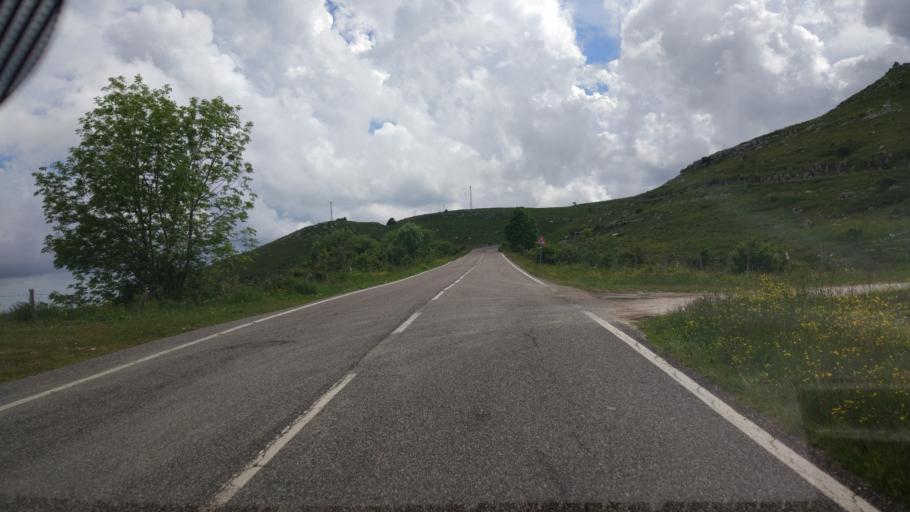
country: IT
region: Veneto
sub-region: Provincia di Verona
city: Bosco Chiesanuova
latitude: 45.6835
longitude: 11.0742
